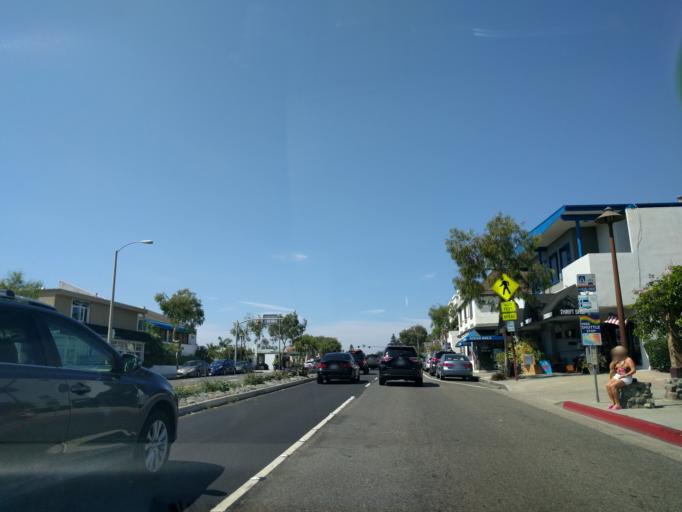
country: US
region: California
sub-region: Orange County
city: Laguna Niguel
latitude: 33.5023
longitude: -117.7442
